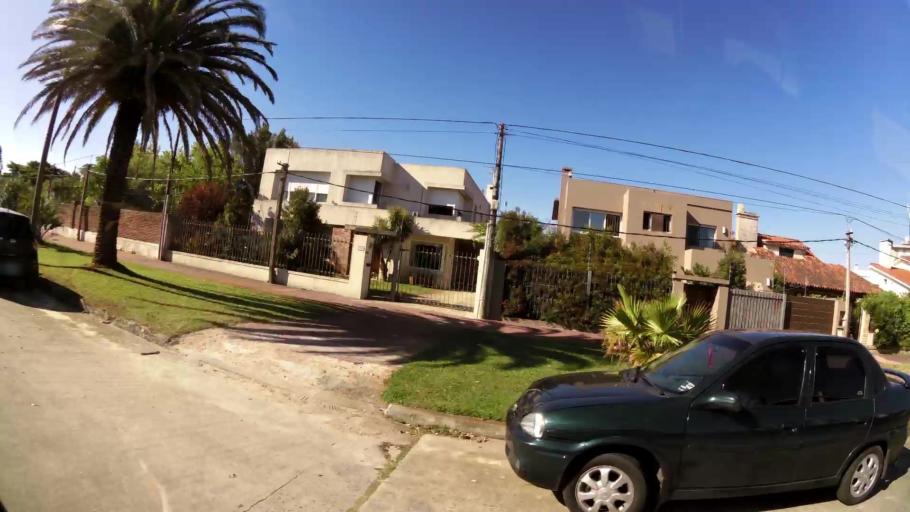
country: UY
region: Canelones
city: Paso de Carrasco
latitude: -34.8926
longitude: -56.0608
